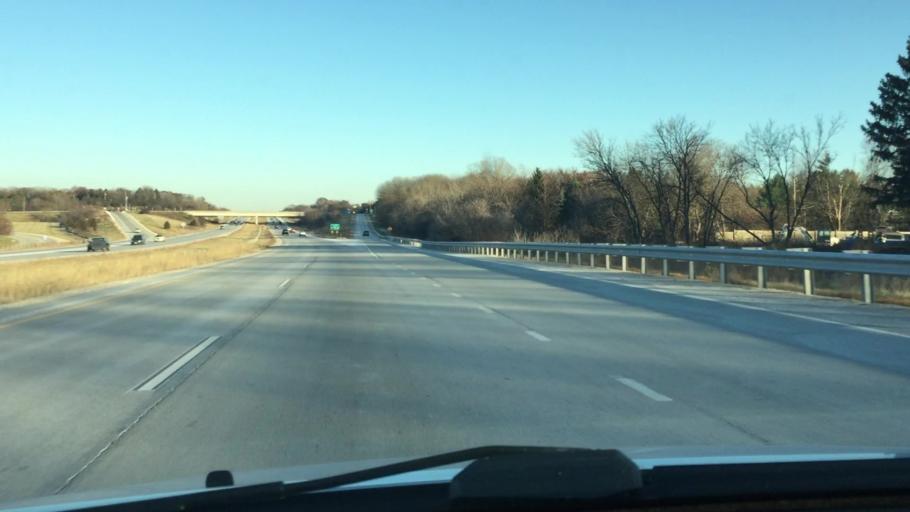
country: US
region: Wisconsin
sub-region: Waukesha County
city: Nashotah
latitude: 43.1015
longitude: -88.4103
